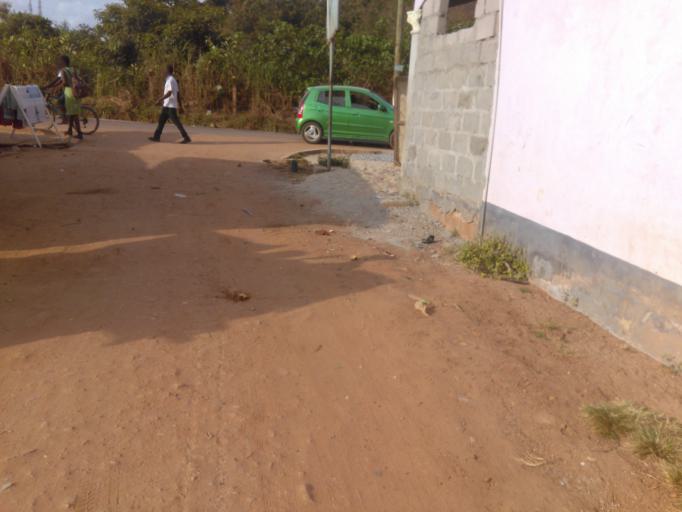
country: GH
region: Central
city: Cape Coast
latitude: 5.1148
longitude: -1.2967
